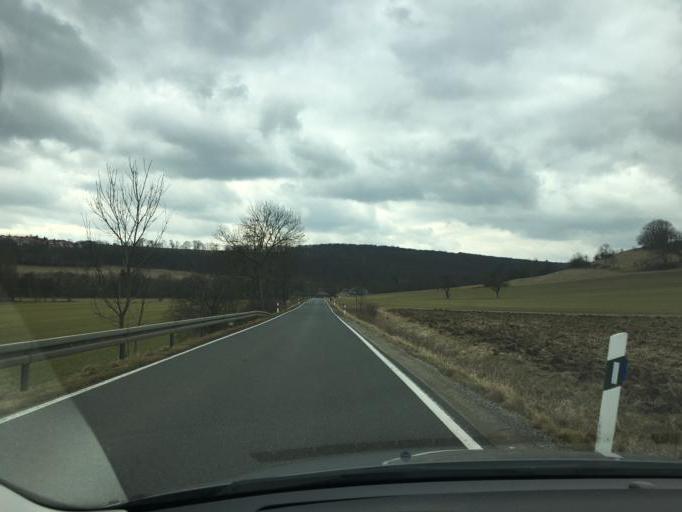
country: DE
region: Thuringia
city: Kiliansroda
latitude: 50.9257
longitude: 11.3763
